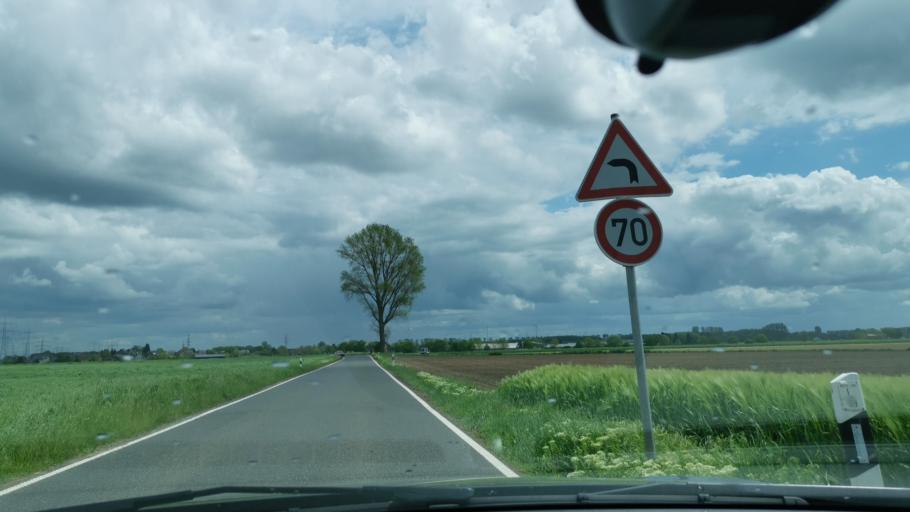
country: DE
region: North Rhine-Westphalia
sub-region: Regierungsbezirk Dusseldorf
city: Rommerskirchen
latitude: 51.0872
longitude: 6.6749
